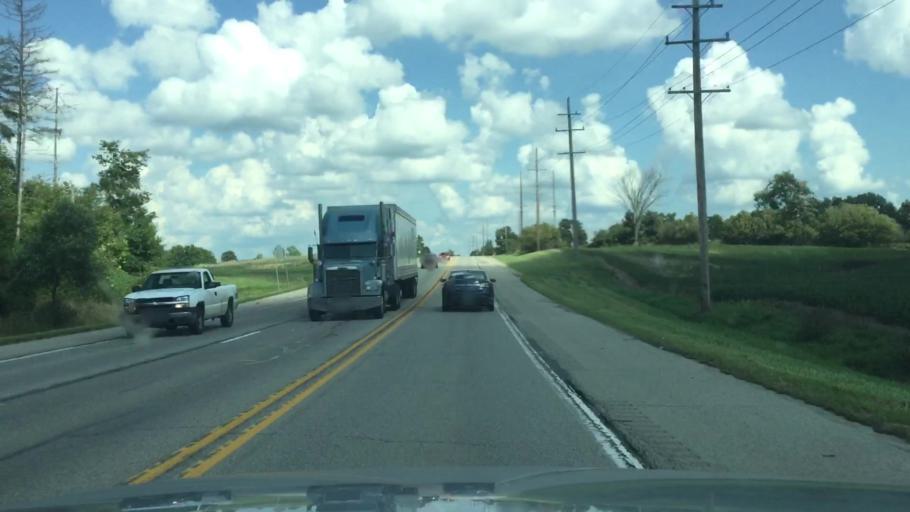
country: US
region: Michigan
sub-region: Washtenaw County
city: Saline
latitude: 42.1392
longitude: -83.8470
